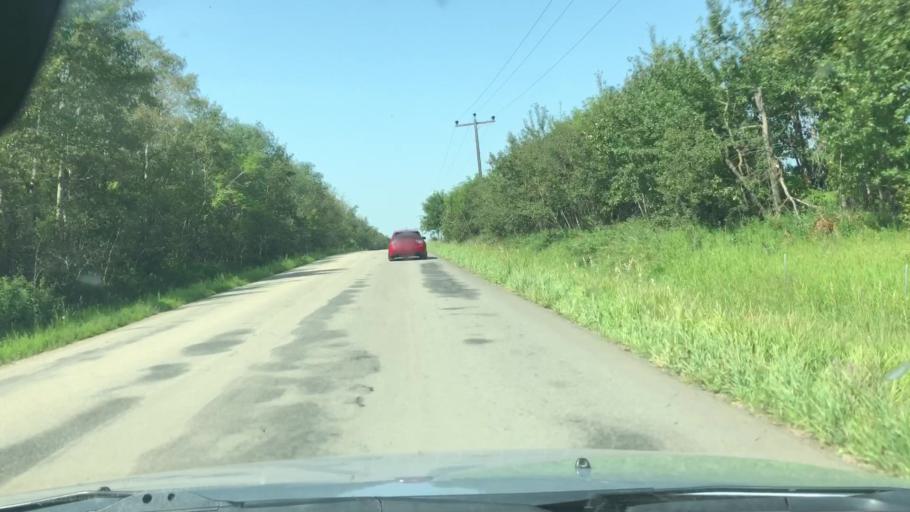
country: CA
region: Alberta
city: Devon
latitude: 53.5122
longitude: -113.7254
